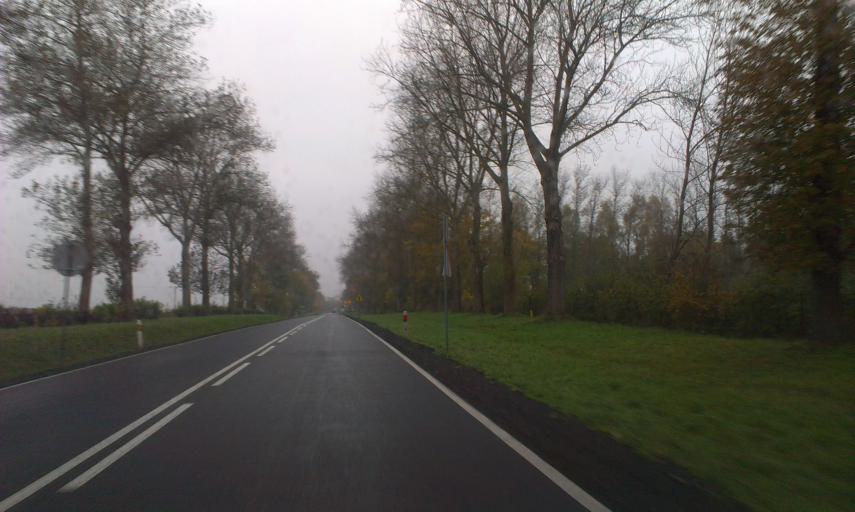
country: PL
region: West Pomeranian Voivodeship
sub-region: Koszalin
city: Koszalin
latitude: 54.1468
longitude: 16.2479
